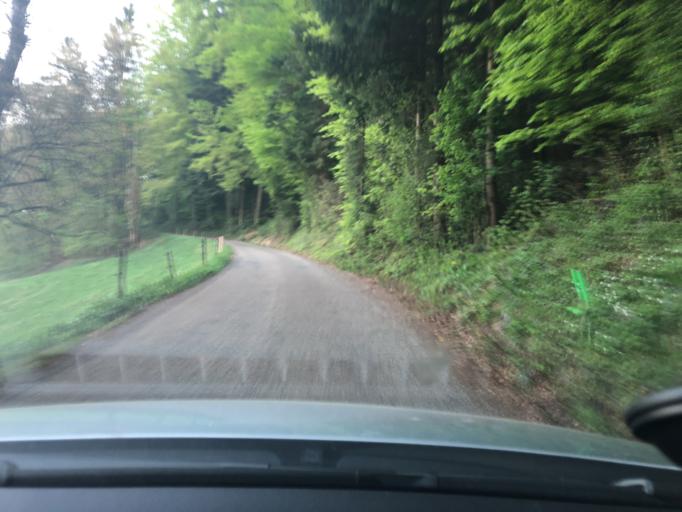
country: DE
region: Baden-Wuerttemberg
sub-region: Freiburg Region
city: Waldshut-Tiengen
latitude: 47.6513
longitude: 8.1957
